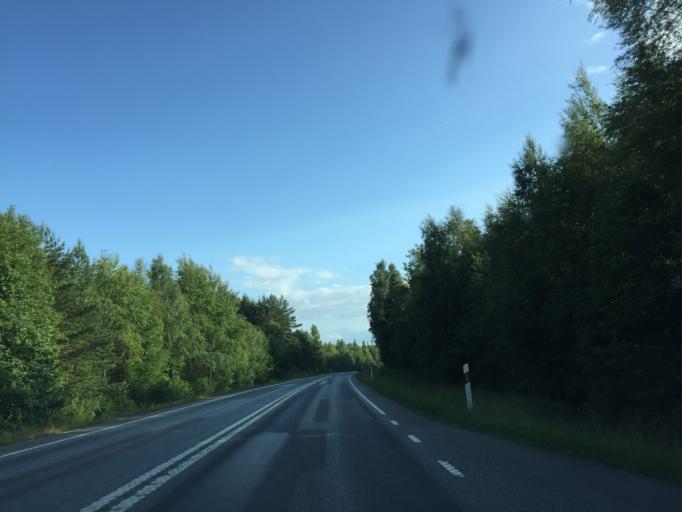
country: SE
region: OEstergoetland
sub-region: Motala Kommun
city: Ryd
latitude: 58.6699
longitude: 14.9688
